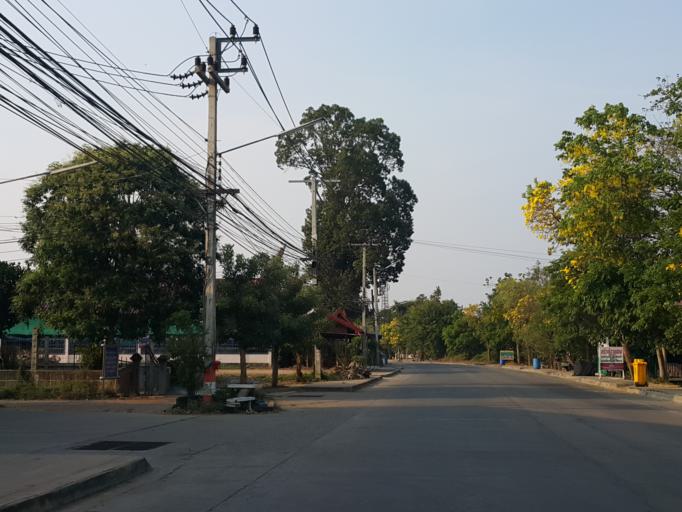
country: TH
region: Chai Nat
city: Sankhaburi
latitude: 15.0555
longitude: 100.1615
